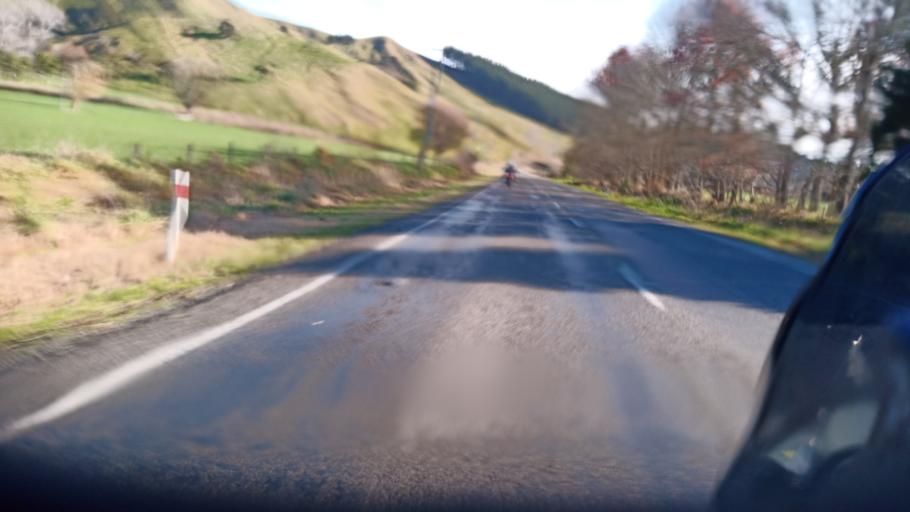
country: NZ
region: Gisborne
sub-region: Gisborne District
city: Gisborne
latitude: -38.4786
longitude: 177.8425
